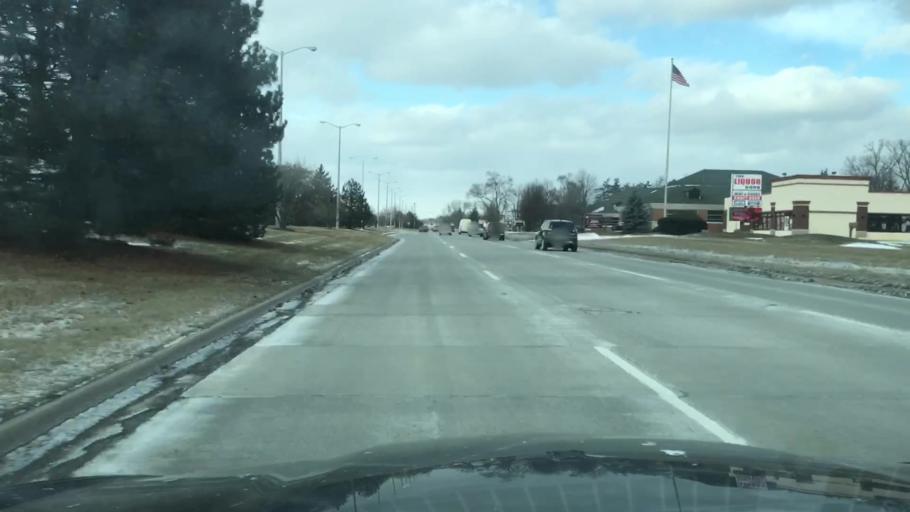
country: US
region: Michigan
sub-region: Macomb County
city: Utica
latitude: 42.6147
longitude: -83.0515
